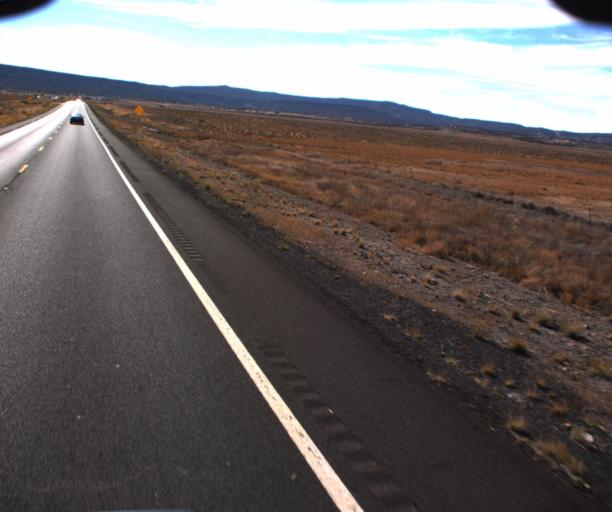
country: US
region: Arizona
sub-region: Coconino County
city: Kaibito
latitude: 36.4759
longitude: -110.7004
